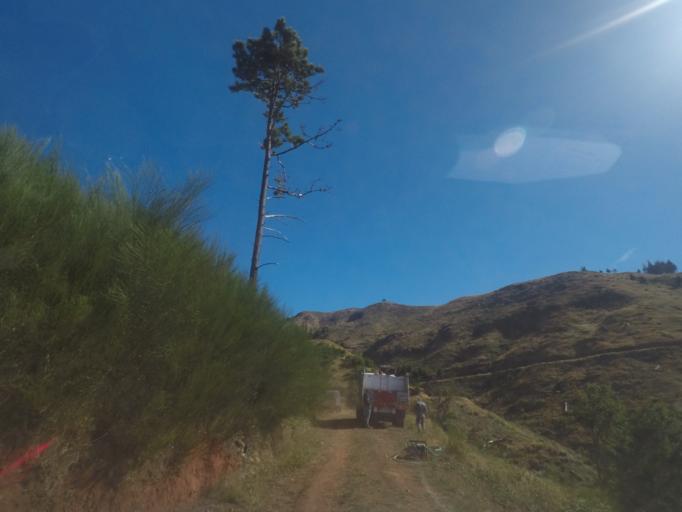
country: PT
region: Madeira
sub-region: Funchal
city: Nossa Senhora do Monte
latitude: 32.7073
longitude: -16.9030
